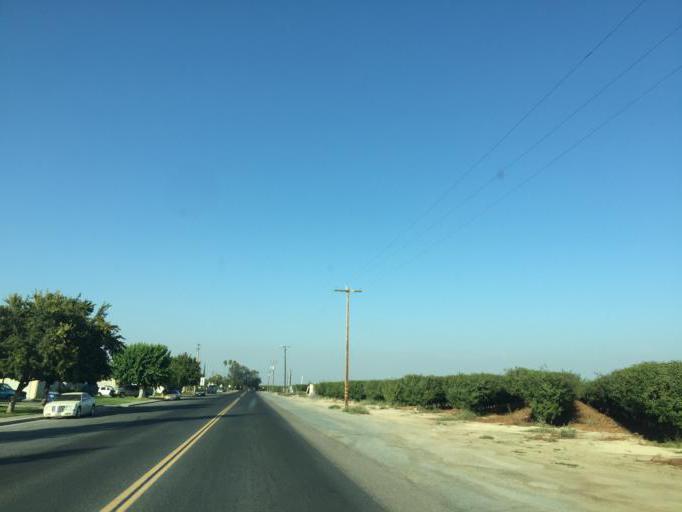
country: US
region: California
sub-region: Tulare County
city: London
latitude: 36.4568
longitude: -119.4802
